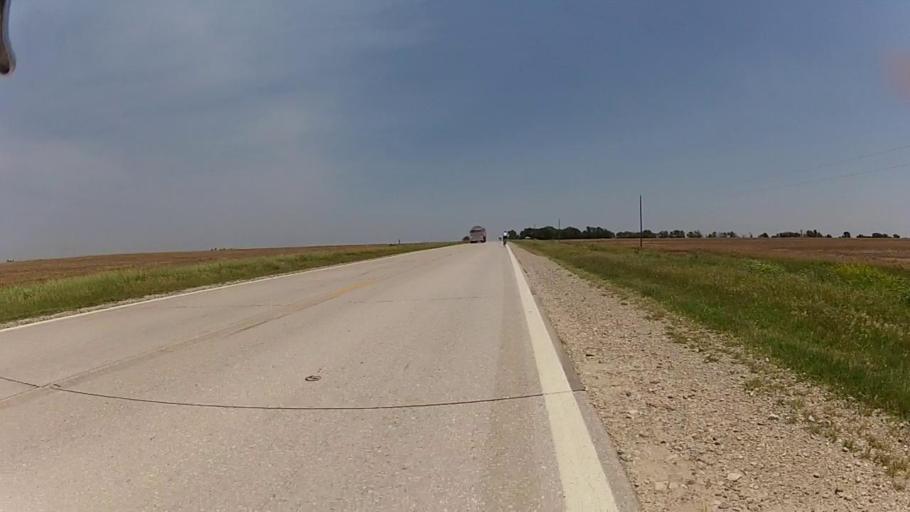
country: US
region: Kansas
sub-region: Sumner County
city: Wellington
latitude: 37.0573
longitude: -97.3608
